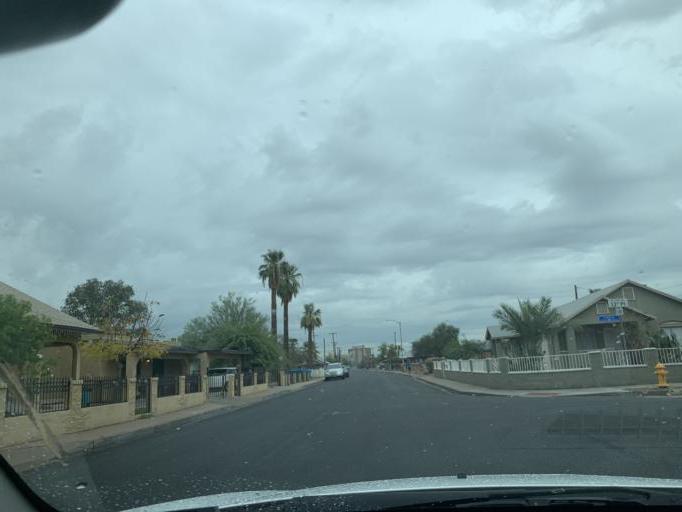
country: US
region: Arizona
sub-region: Maricopa County
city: Phoenix
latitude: 33.4539
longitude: -112.0539
